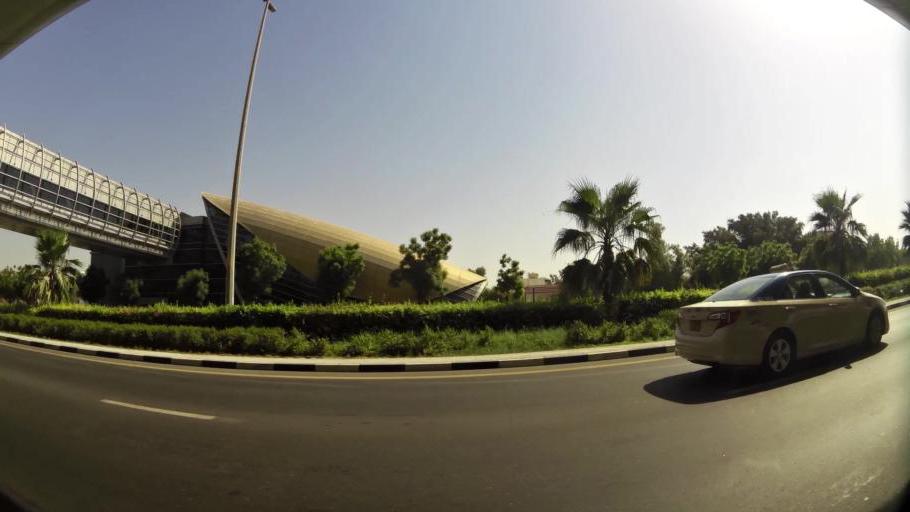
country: AE
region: Ash Shariqah
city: Sharjah
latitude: 25.2733
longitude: 55.3690
